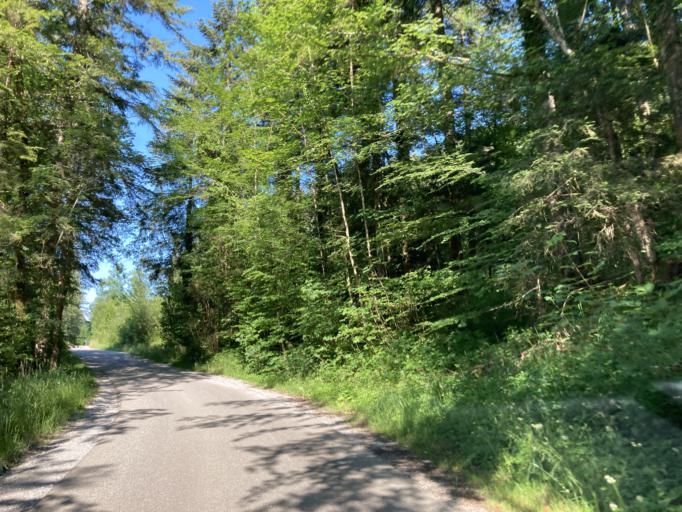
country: DE
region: Bavaria
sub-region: Upper Bavaria
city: Nussdorf am Inn
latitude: 47.7467
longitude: 12.1827
